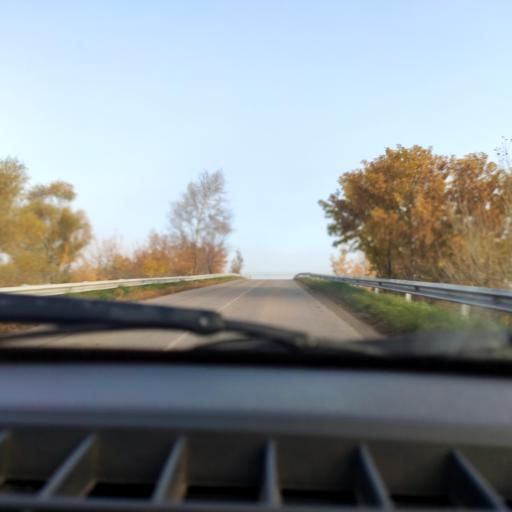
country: RU
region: Bashkortostan
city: Avdon
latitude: 54.6506
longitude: 55.7780
